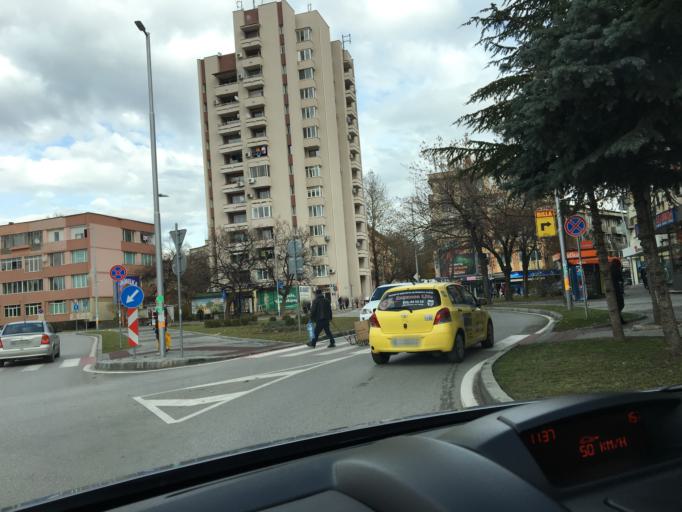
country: BG
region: Blagoevgrad
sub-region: Obshtina Blagoevgrad
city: Blagoevgrad
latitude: 42.0168
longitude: 23.0945
